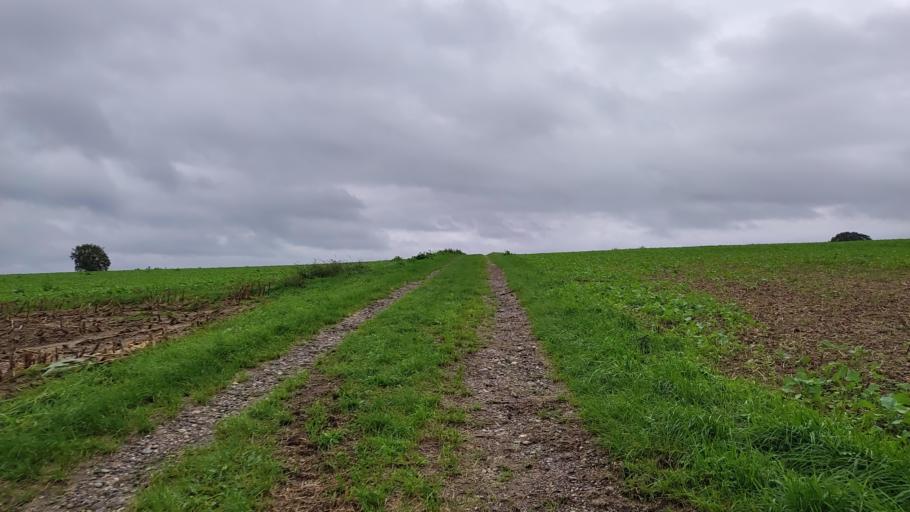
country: DE
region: Bavaria
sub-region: Swabia
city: Altenmunster
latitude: 48.4503
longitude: 10.6197
